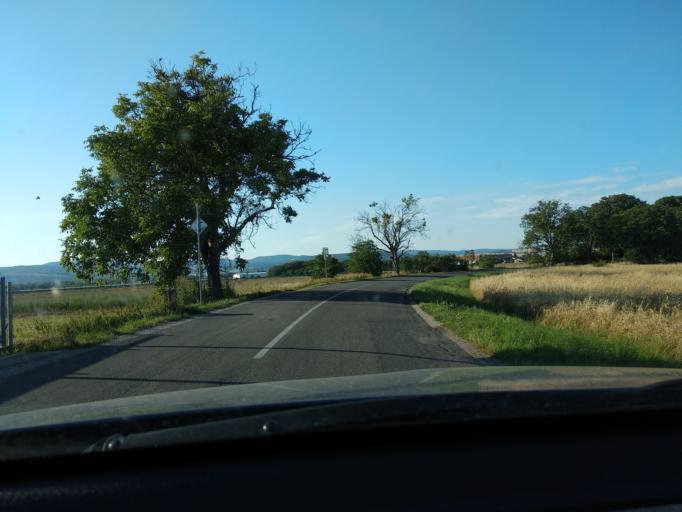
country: SK
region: Trenciansky
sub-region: Okres Trencin
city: Trencin
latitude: 48.8637
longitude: 18.0171
